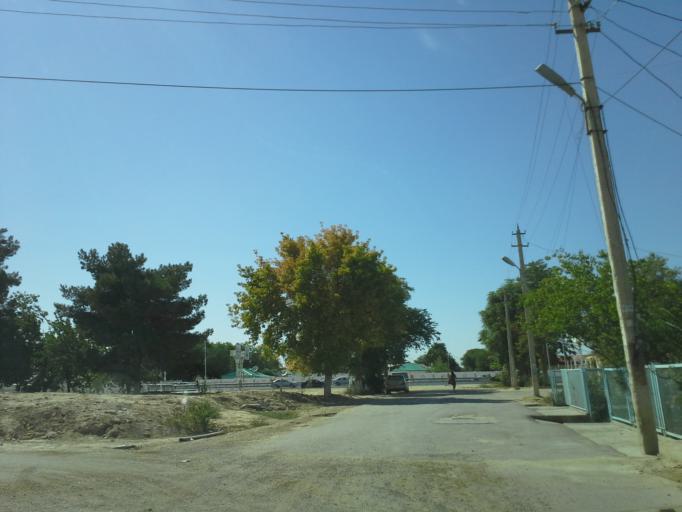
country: TM
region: Ahal
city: Ashgabat
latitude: 37.9420
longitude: 58.4041
